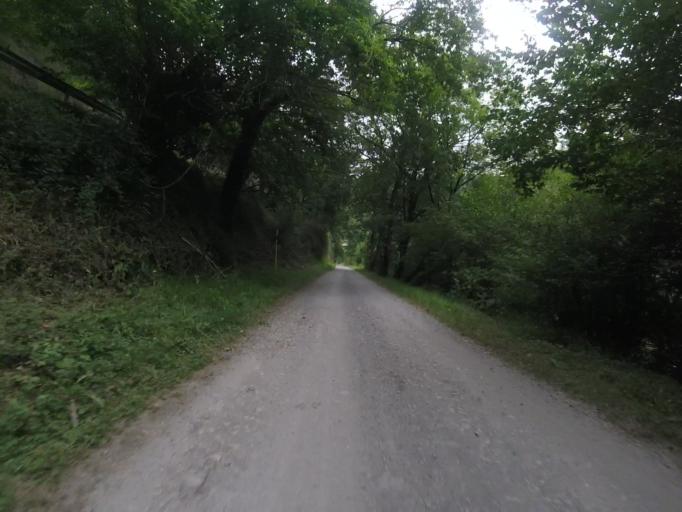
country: ES
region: Navarre
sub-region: Provincia de Navarra
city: Sunbilla
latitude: 43.1903
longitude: -1.6703
